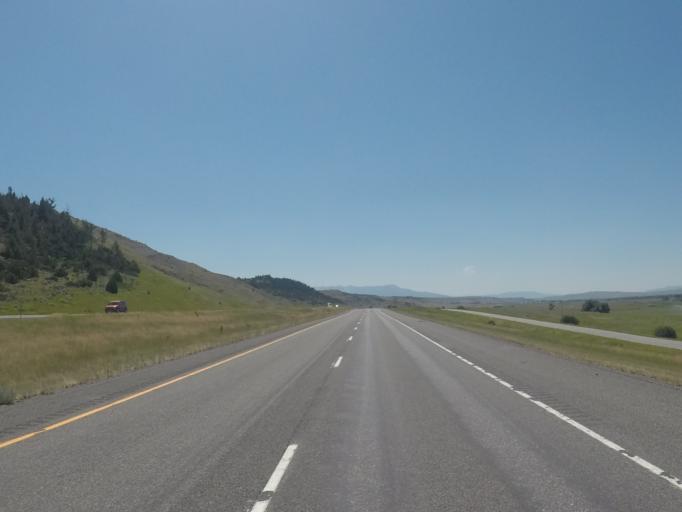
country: US
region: Montana
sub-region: Sweet Grass County
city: Big Timber
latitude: 45.7734
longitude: -110.0759
